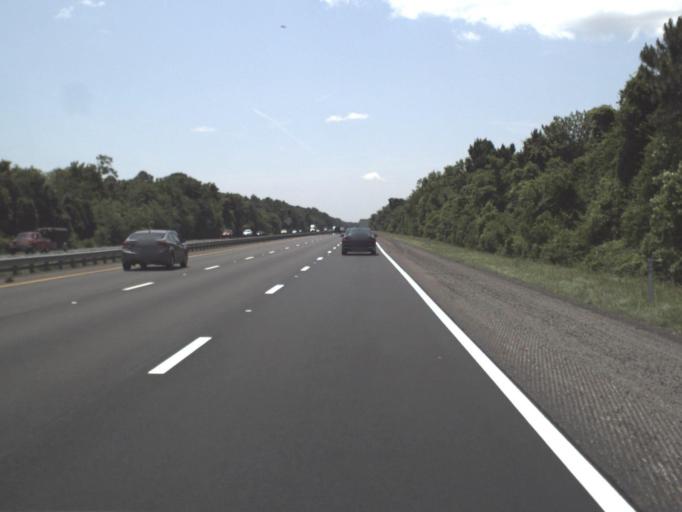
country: US
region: Florida
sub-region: Nassau County
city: Yulee
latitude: 30.5695
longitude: -81.6445
